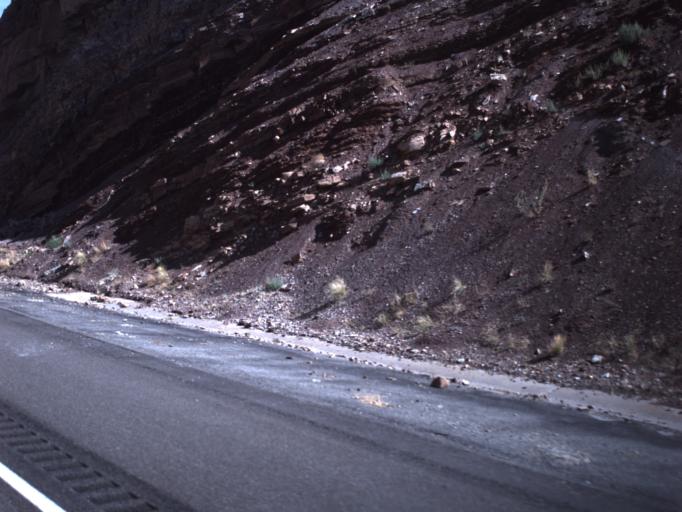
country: US
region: Utah
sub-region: Carbon County
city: East Carbon City
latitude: 38.9240
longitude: -110.4483
